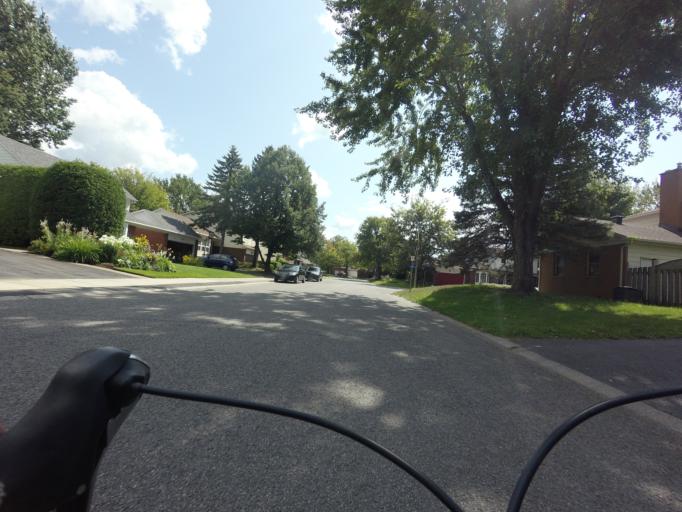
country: CA
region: Ontario
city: Bells Corners
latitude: 45.2833
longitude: -75.8617
